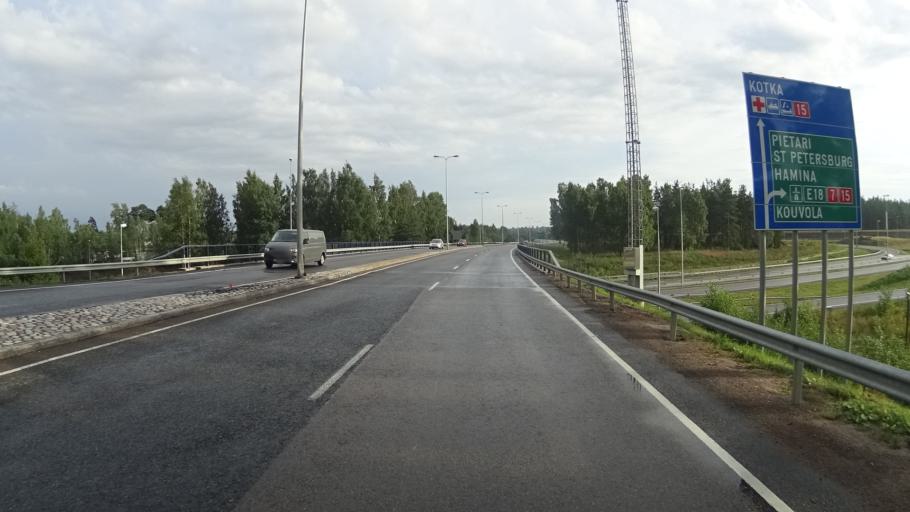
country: FI
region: Kymenlaakso
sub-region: Kotka-Hamina
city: Karhula
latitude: 60.5053
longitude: 26.8980
